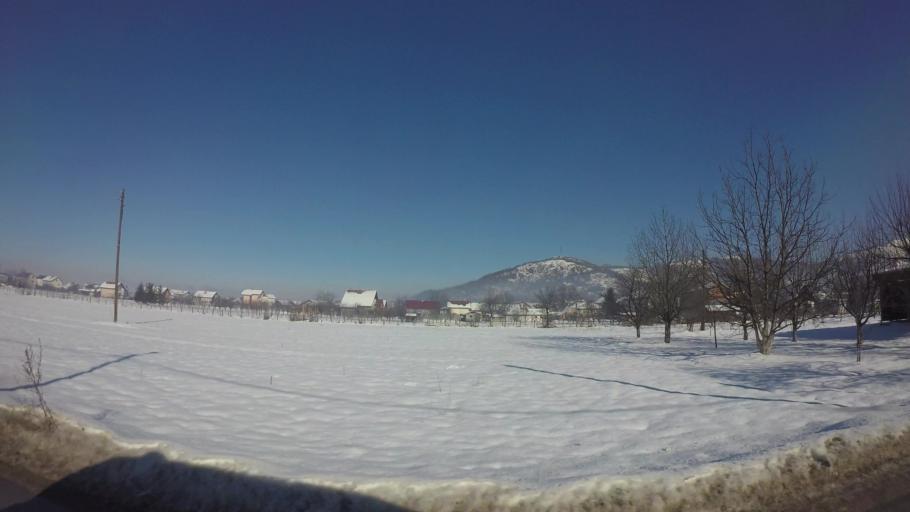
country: BA
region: Federation of Bosnia and Herzegovina
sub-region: Kanton Sarajevo
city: Sarajevo
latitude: 43.7963
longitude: 18.3465
